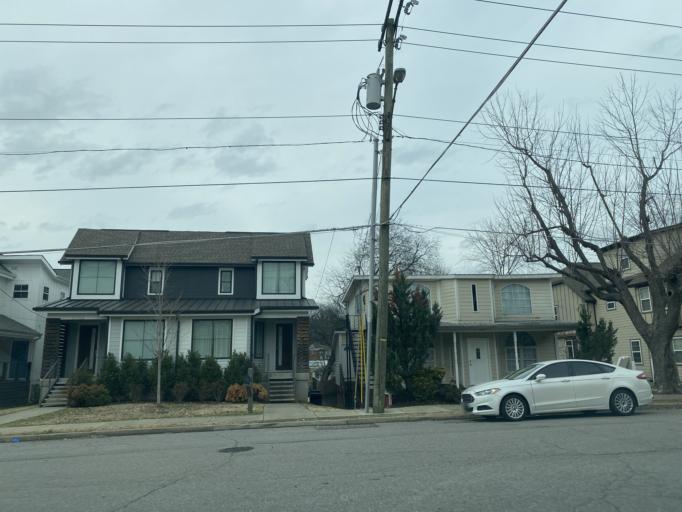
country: US
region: Tennessee
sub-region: Davidson County
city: Nashville
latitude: 36.1371
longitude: -86.7905
